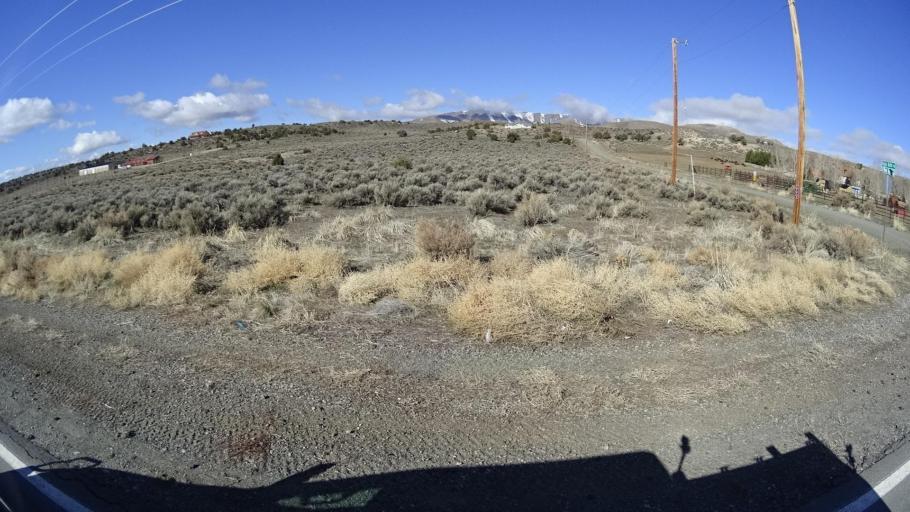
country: US
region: Nevada
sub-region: Washoe County
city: Cold Springs
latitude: 39.7534
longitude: -119.8859
